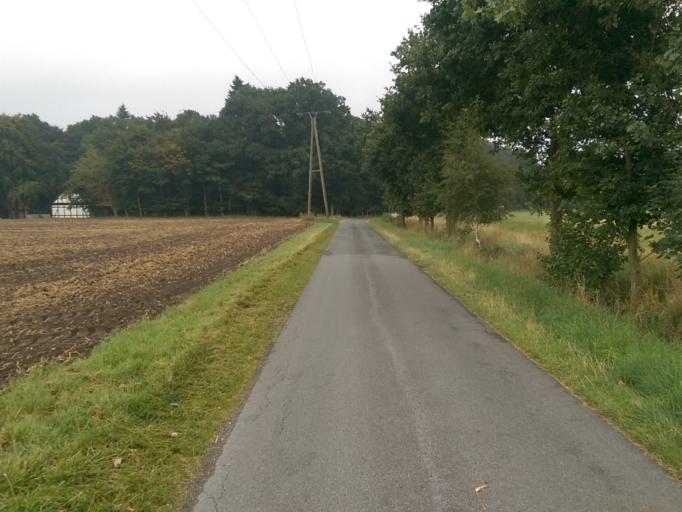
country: DE
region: North Rhine-Westphalia
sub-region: Regierungsbezirk Detmold
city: Harsewinkel
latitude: 51.9224
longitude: 8.2572
